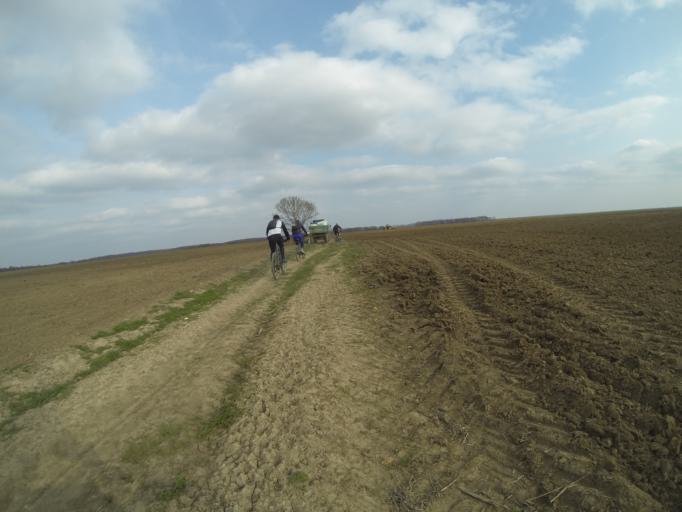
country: RO
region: Dolj
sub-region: Comuna Bucovat
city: Bucovat
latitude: 44.2470
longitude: 23.7140
